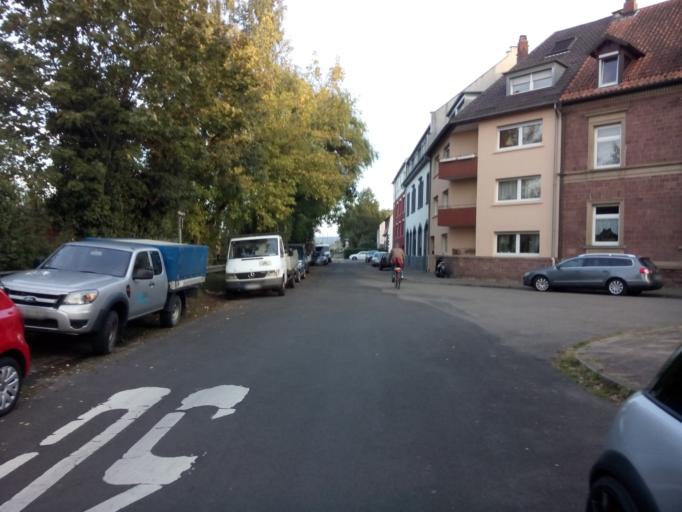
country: DE
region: Baden-Wuerttemberg
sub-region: Karlsruhe Region
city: Karlsruhe
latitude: 49.0061
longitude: 8.3583
